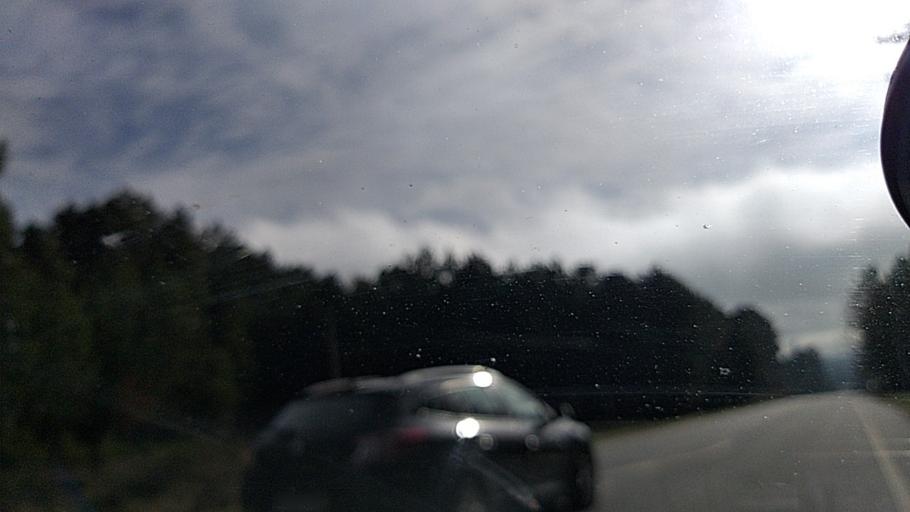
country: PT
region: Guarda
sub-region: Aguiar da Beira
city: Aguiar da Beira
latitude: 40.7944
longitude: -7.5166
